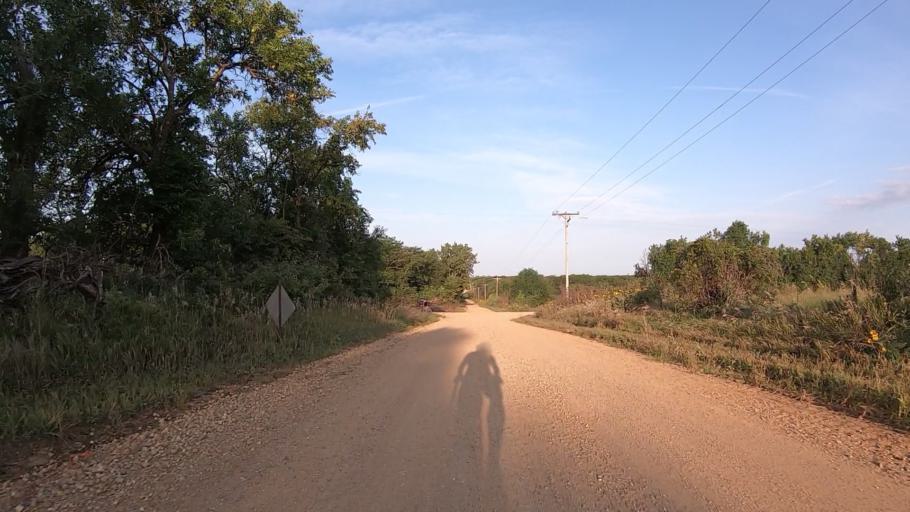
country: US
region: Kansas
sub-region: Marshall County
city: Marysville
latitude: 39.7693
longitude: -96.7502
